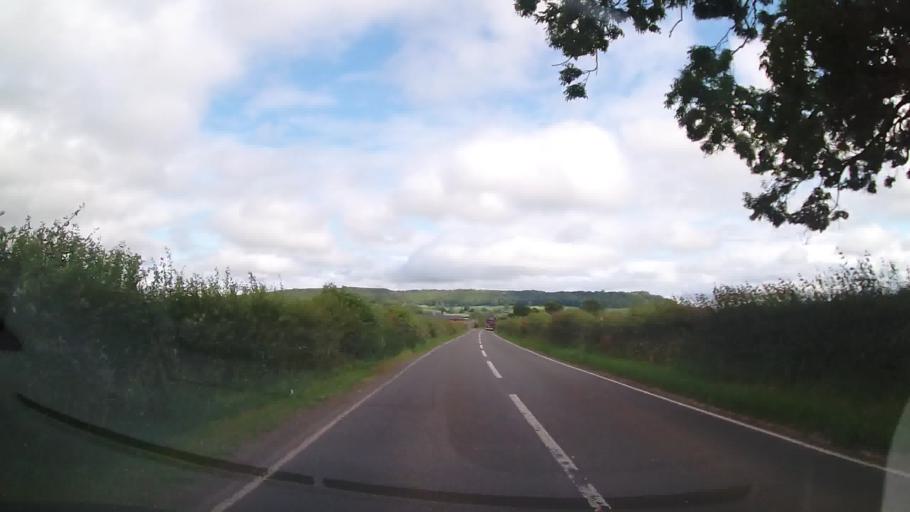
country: GB
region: England
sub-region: Shropshire
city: Pant
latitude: 52.8005
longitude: -3.1249
